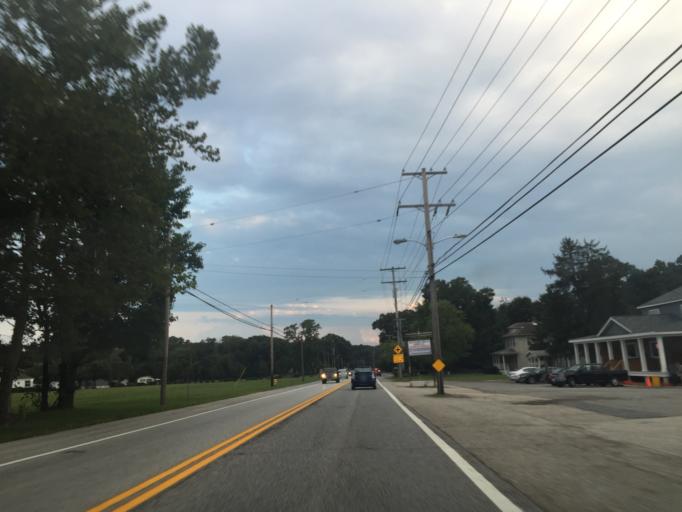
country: US
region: Maryland
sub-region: Anne Arundel County
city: Severn
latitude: 39.1293
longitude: -76.6891
